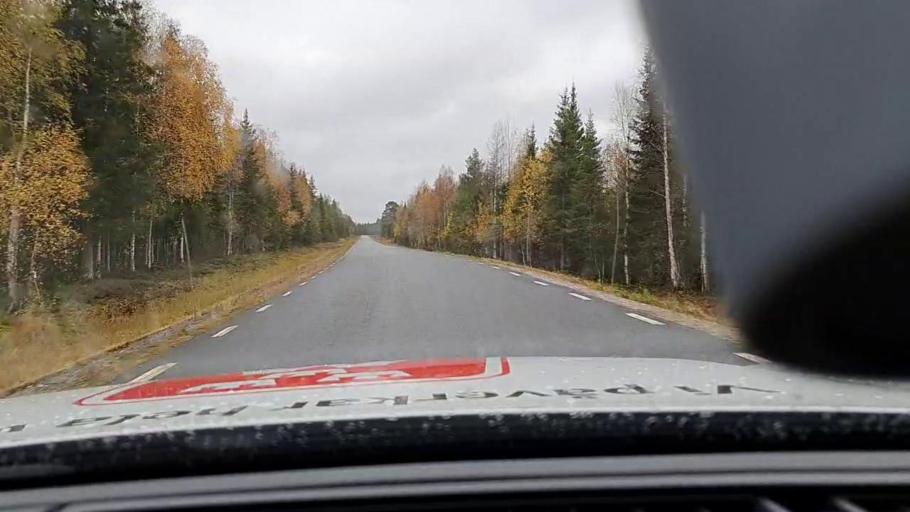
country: SE
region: Norrbotten
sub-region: Haparanda Kommun
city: Haparanda
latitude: 65.9342
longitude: 23.8136
